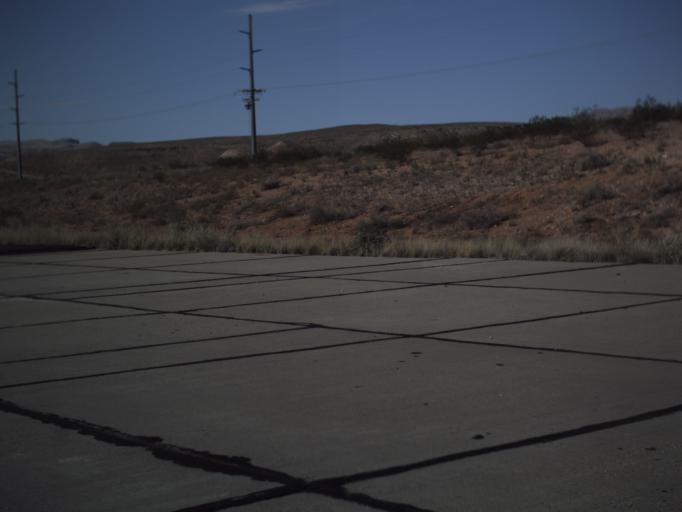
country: US
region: Utah
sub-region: Washington County
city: Saint George
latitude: 37.0156
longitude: -113.6143
